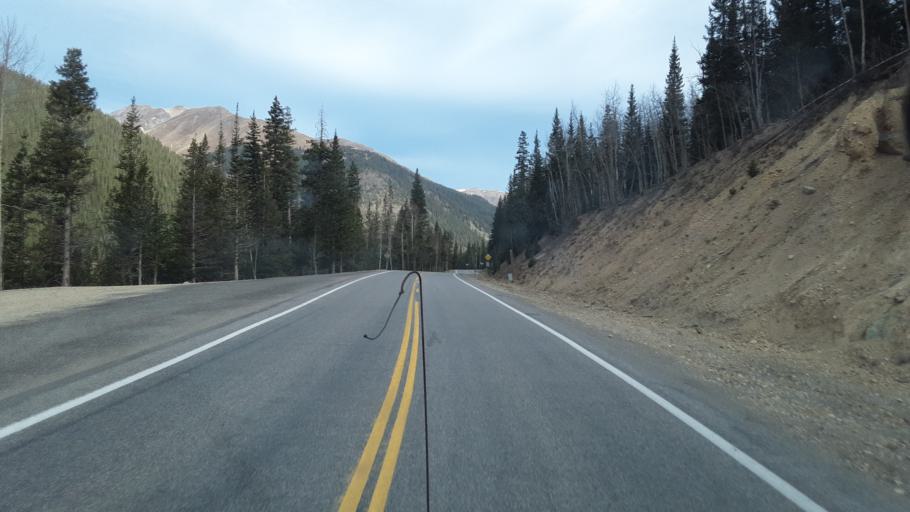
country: US
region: Colorado
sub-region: San Juan County
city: Silverton
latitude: 37.8324
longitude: -107.7239
